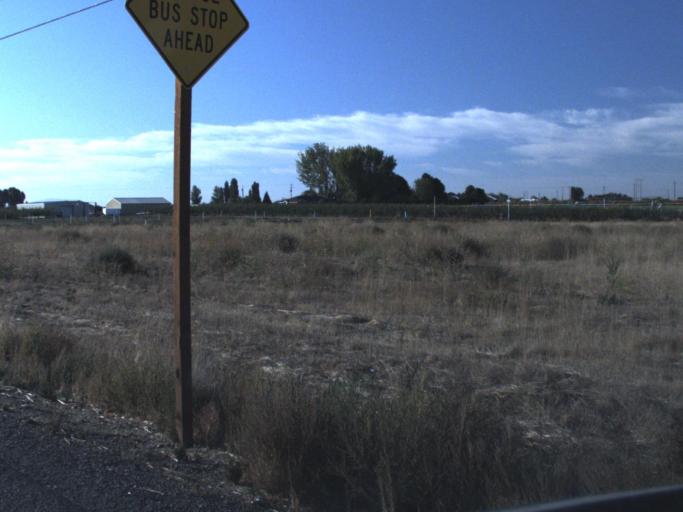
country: US
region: Washington
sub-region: Walla Walla County
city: Burbank
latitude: 46.2118
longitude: -118.9666
